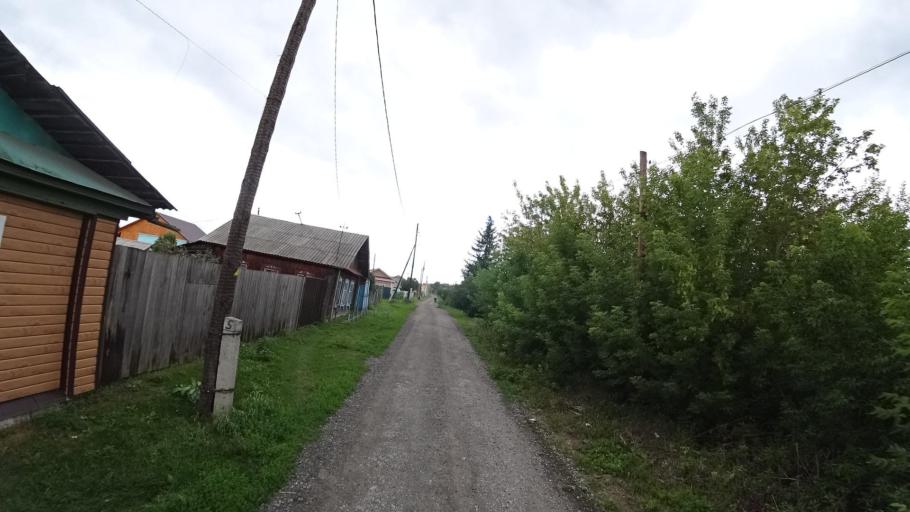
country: RU
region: Sverdlovsk
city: Kamyshlov
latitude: 56.8518
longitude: 62.6895
